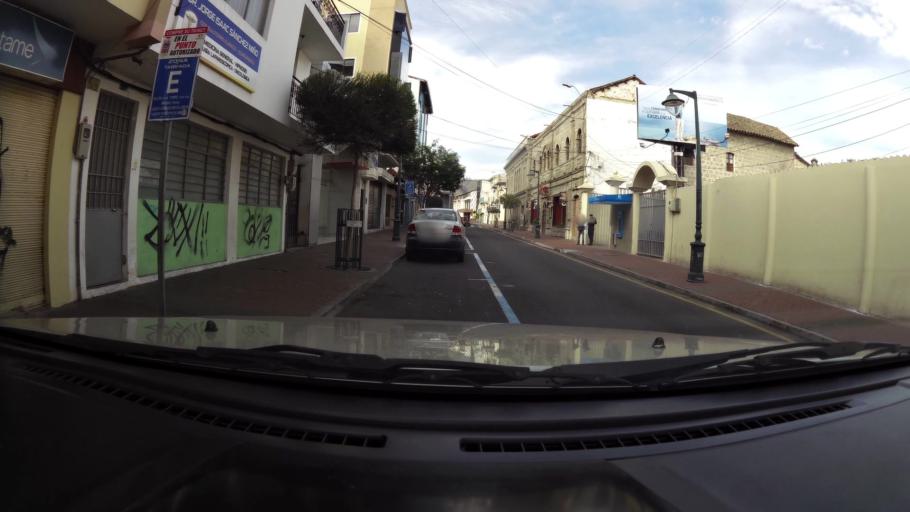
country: EC
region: Tungurahua
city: Ambato
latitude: -1.2424
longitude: -78.6253
